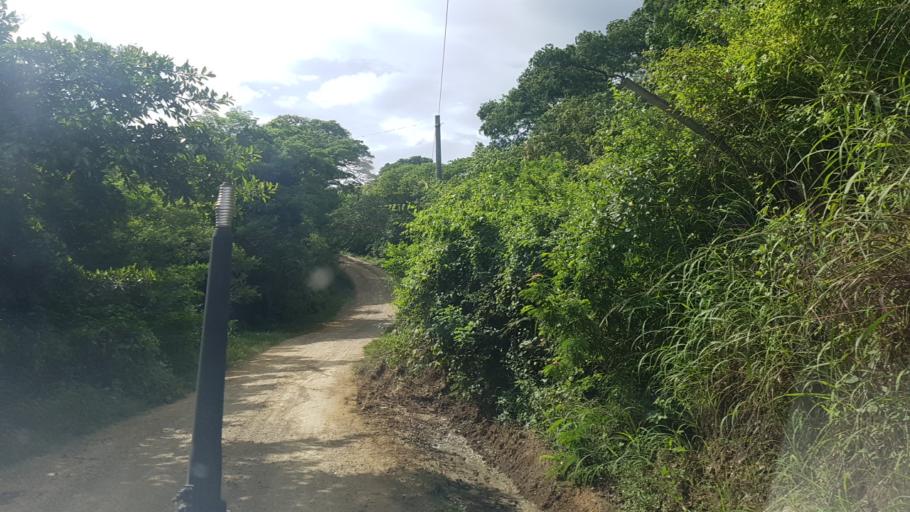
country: HN
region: El Paraiso
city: Oropoli
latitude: 13.7437
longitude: -86.7064
